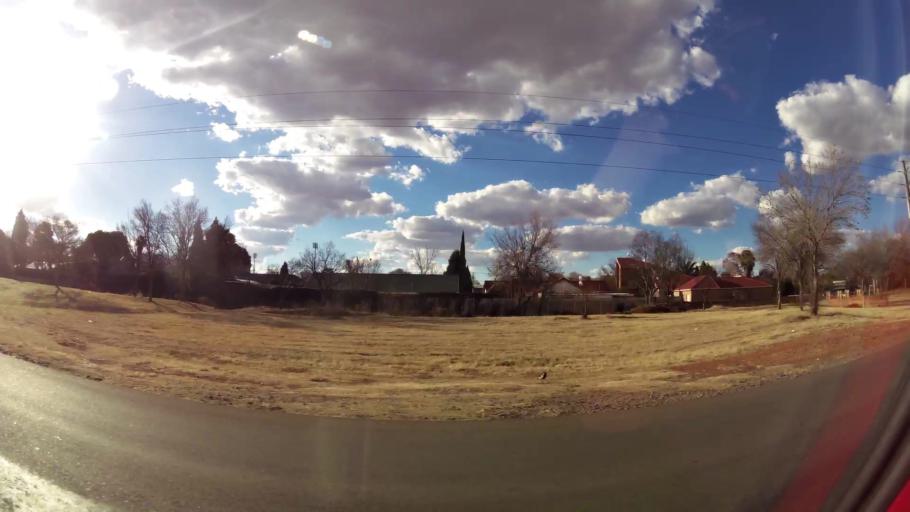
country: ZA
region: North-West
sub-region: Dr Kenneth Kaunda District Municipality
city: Potchefstroom
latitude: -26.7006
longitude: 27.1022
